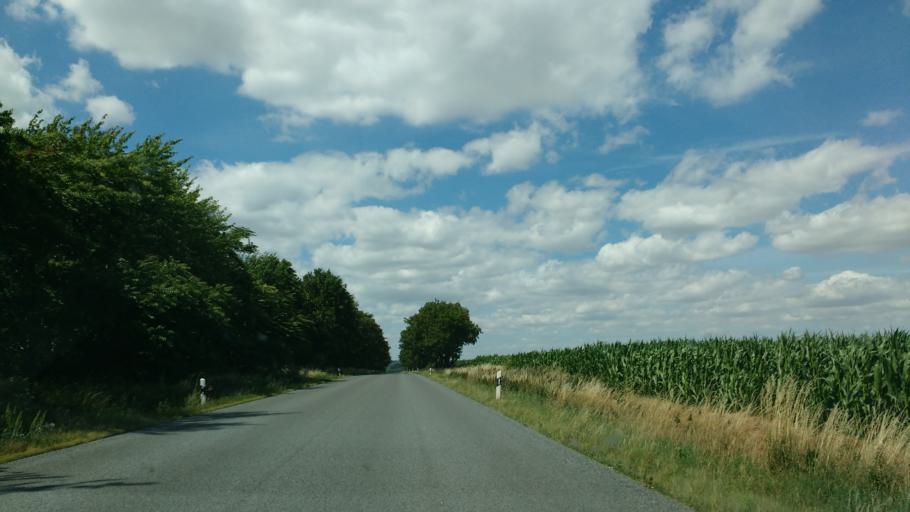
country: DE
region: Saxony-Anhalt
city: Farnstadt
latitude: 51.4166
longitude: 11.5746
